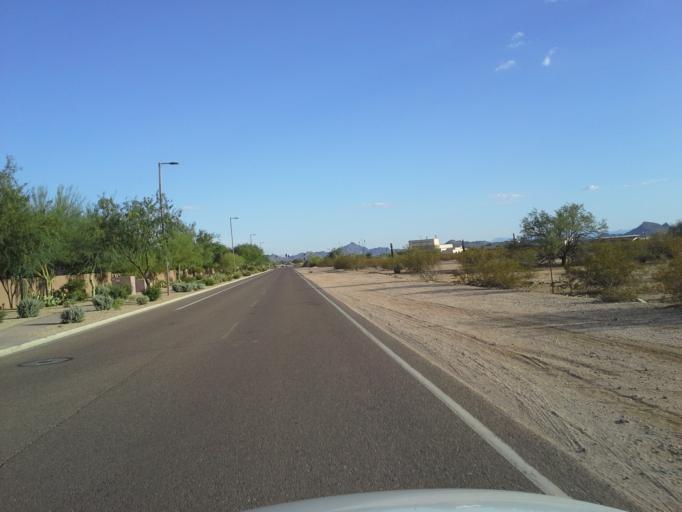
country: US
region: Arizona
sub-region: Maricopa County
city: Cave Creek
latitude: 33.6875
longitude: -112.0051
